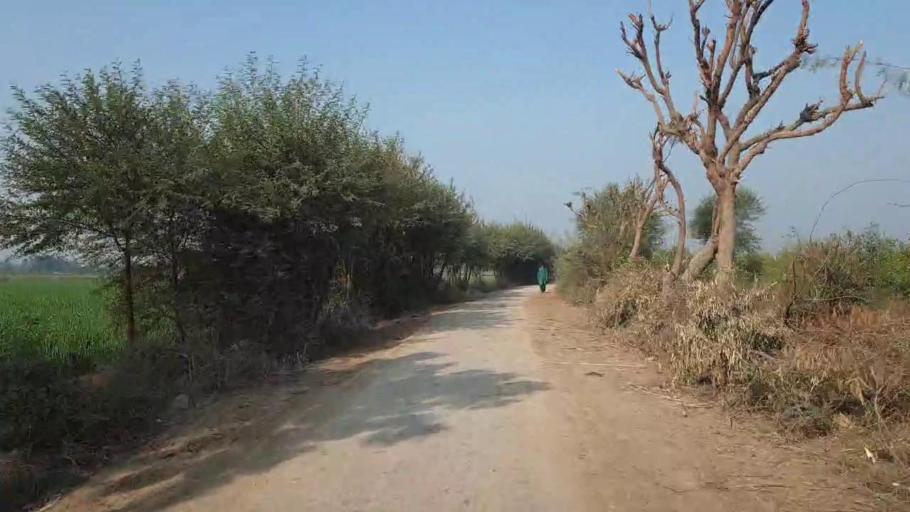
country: PK
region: Sindh
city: Matiari
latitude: 25.6771
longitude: 68.4957
